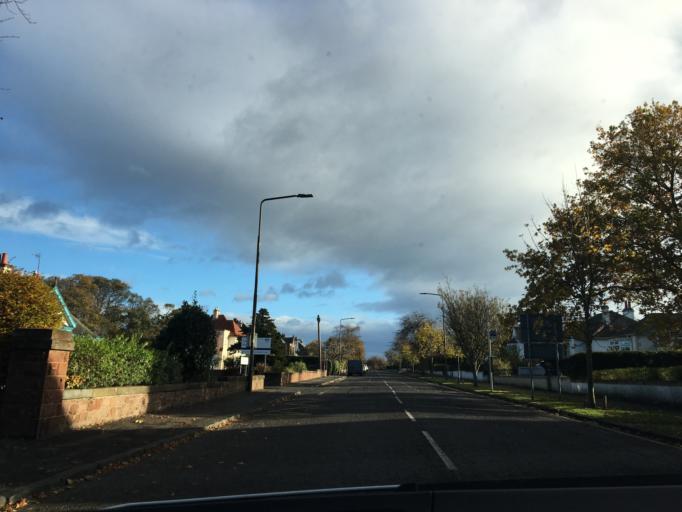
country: GB
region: Scotland
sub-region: East Lothian
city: North Berwick
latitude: 56.0553
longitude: -2.7190
